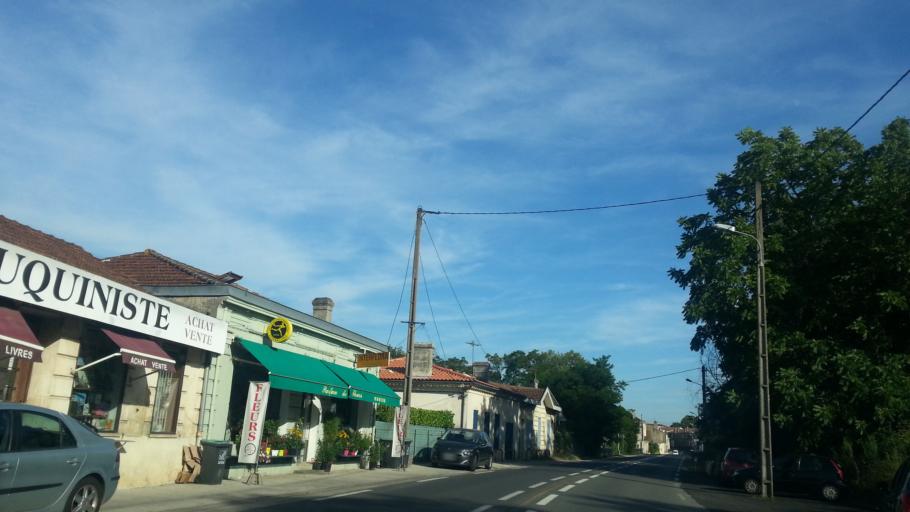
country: FR
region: Aquitaine
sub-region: Departement de la Gironde
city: Beautiran
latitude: 44.6998
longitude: -0.4495
